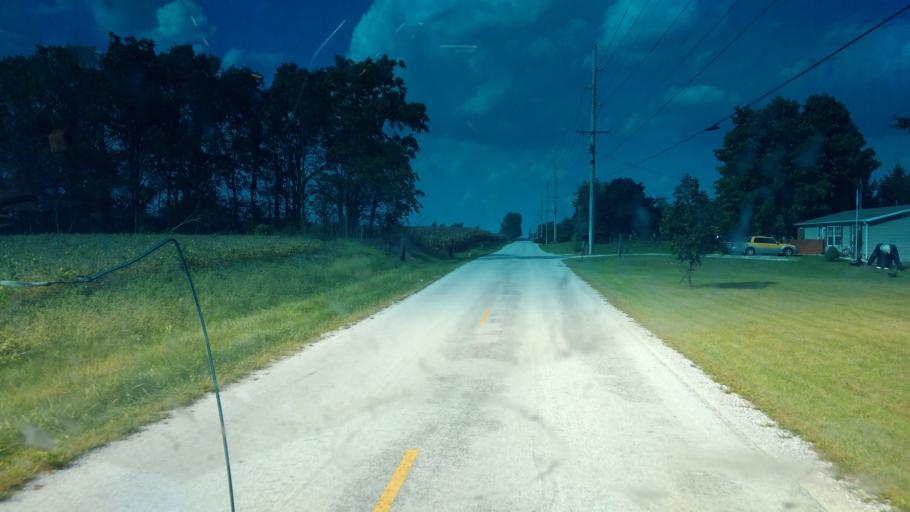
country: US
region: Ohio
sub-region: Hardin County
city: Kenton
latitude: 40.7535
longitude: -83.6524
